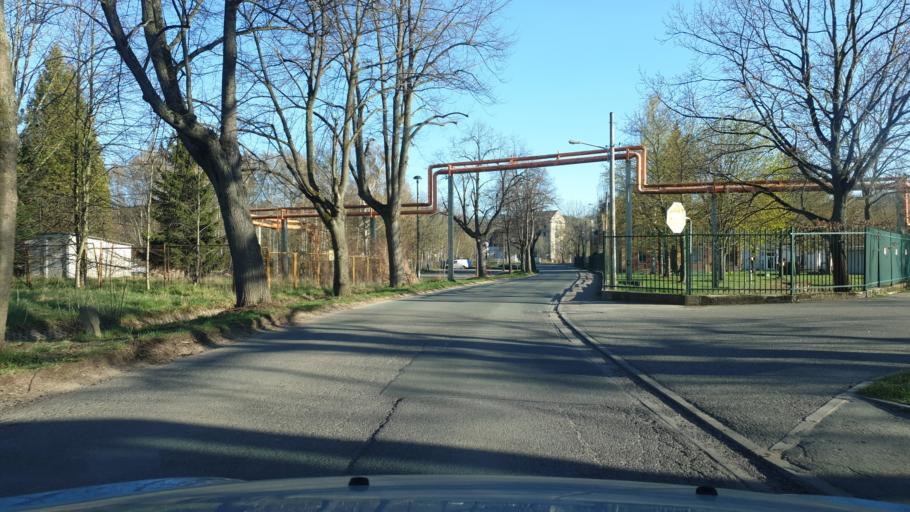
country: DE
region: Saxony
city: Neukirchen
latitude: 50.7739
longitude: 12.9012
